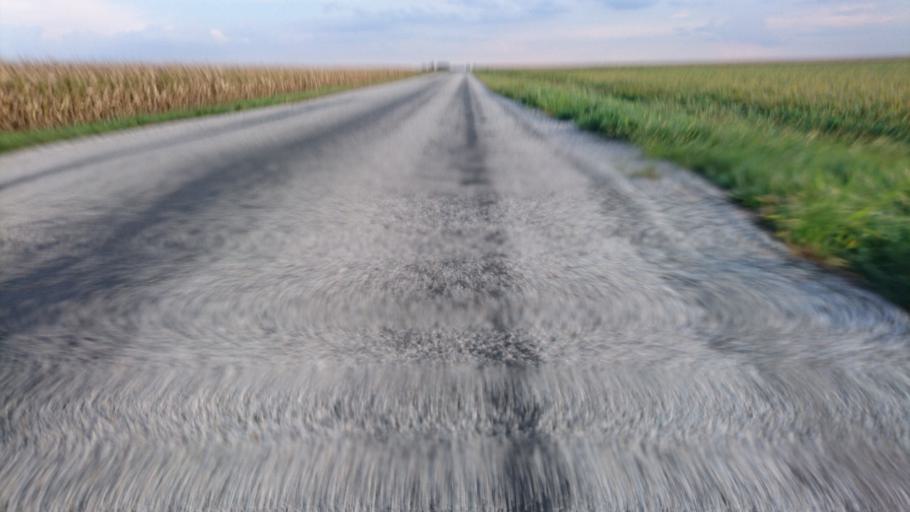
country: US
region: Illinois
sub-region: Logan County
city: Atlanta
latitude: 40.2542
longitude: -89.2052
